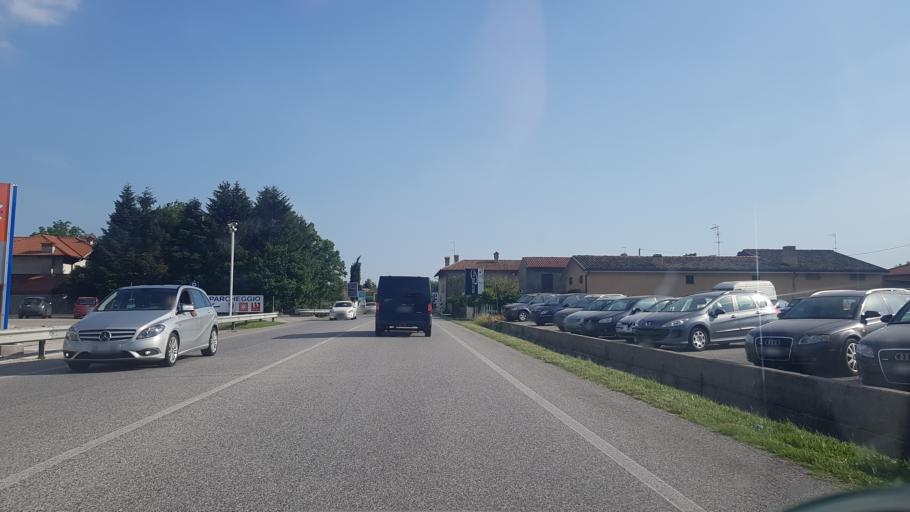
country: IT
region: Friuli Venezia Giulia
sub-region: Provincia di Udine
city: Gemona
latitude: 46.2760
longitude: 13.1087
